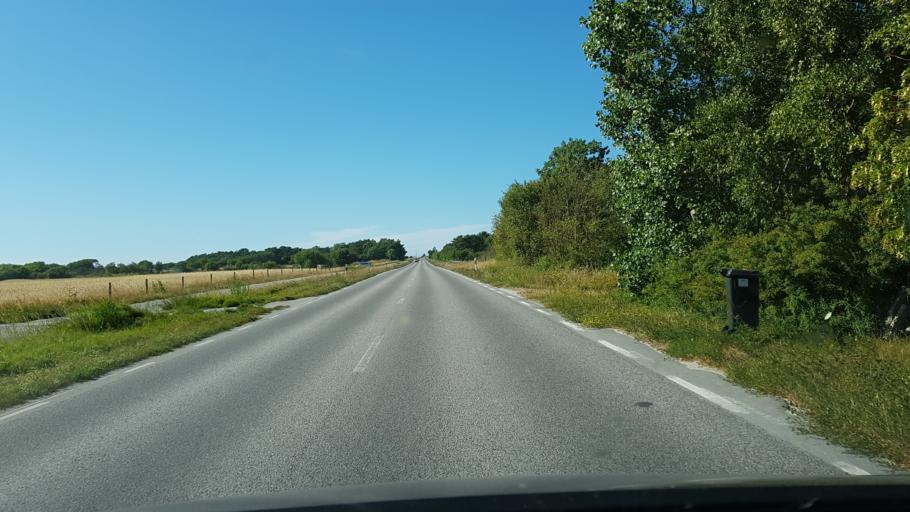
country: SE
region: Gotland
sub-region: Gotland
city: Klintehamn
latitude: 57.4612
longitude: 18.1280
